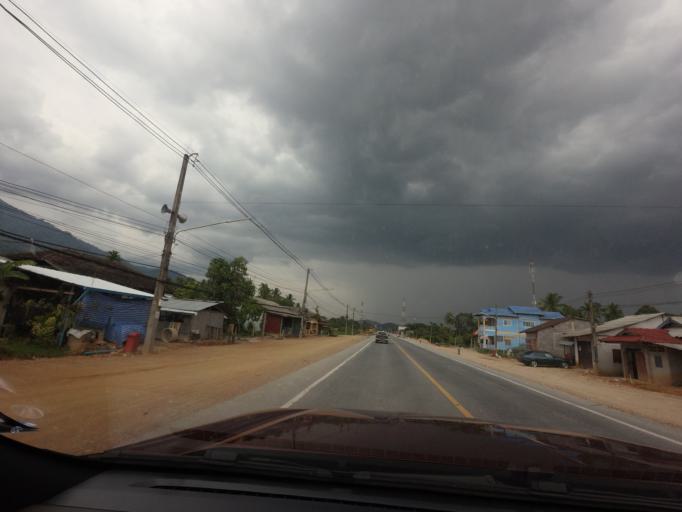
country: TH
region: Yala
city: Krong Pi Nang
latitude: 6.4260
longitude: 101.2779
